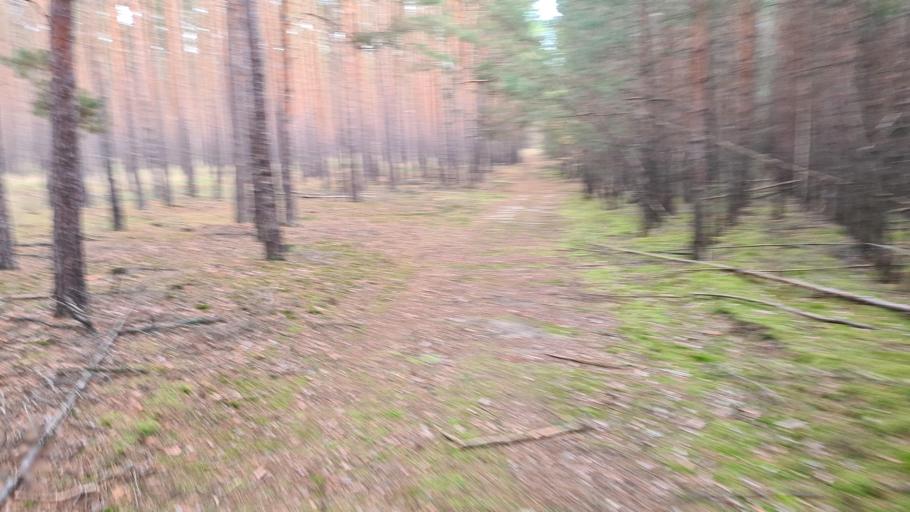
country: DE
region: Brandenburg
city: Trobitz
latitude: 51.5719
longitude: 13.4341
